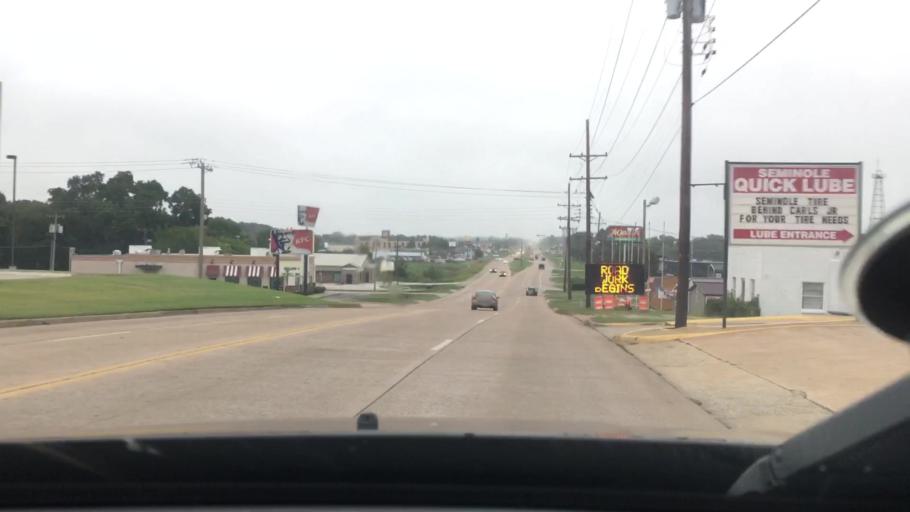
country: US
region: Oklahoma
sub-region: Seminole County
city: Seminole
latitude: 35.2326
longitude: -96.6710
